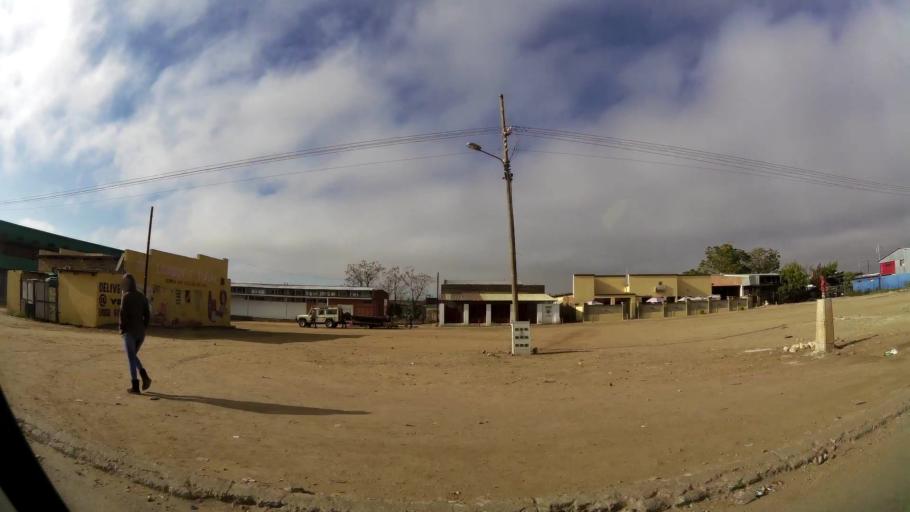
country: ZA
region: Limpopo
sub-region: Capricorn District Municipality
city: Polokwane
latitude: -23.8467
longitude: 29.3902
